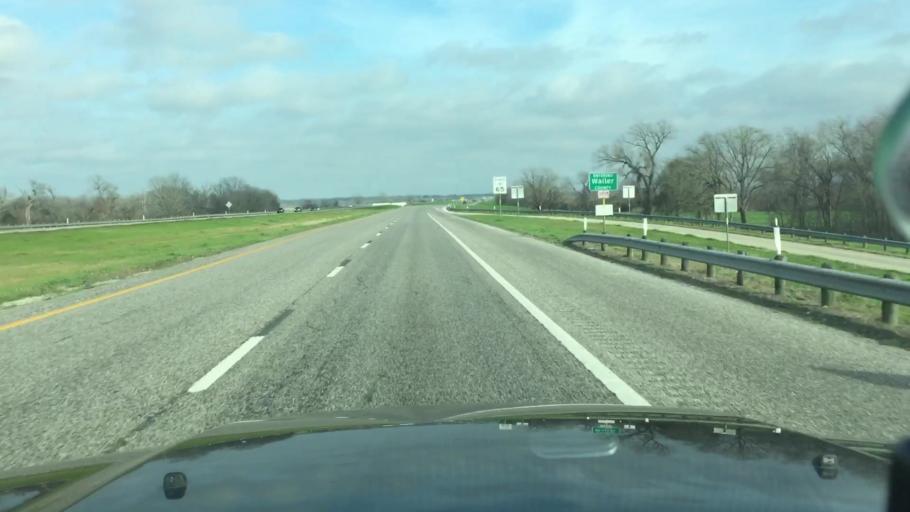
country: US
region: Texas
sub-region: Waller County
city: Hempstead
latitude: 30.1293
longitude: -96.1846
